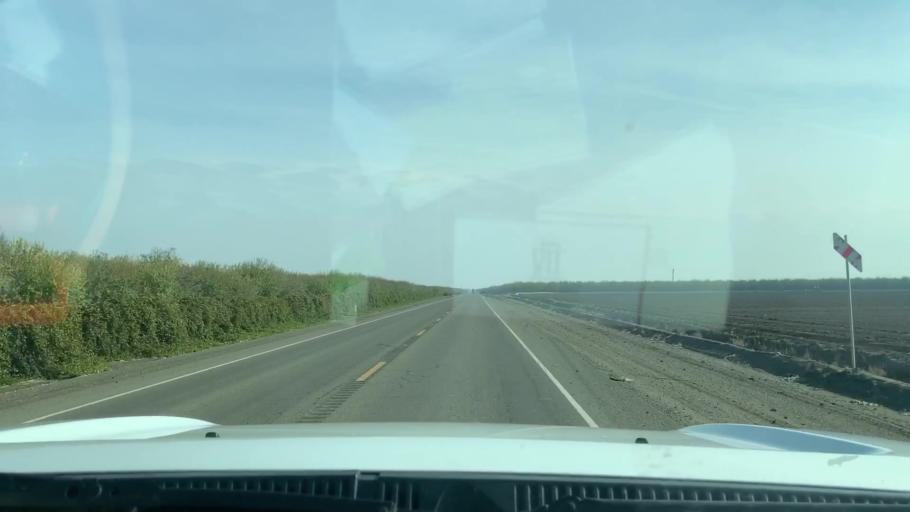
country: US
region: California
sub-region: Fresno County
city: Huron
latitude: 36.2552
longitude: -120.1433
